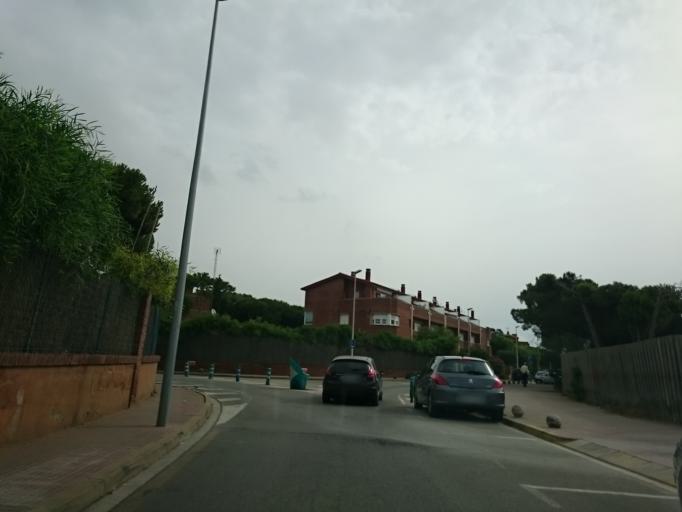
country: ES
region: Catalonia
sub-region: Provincia de Barcelona
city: Castelldefels
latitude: 41.2659
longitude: 2.0056
